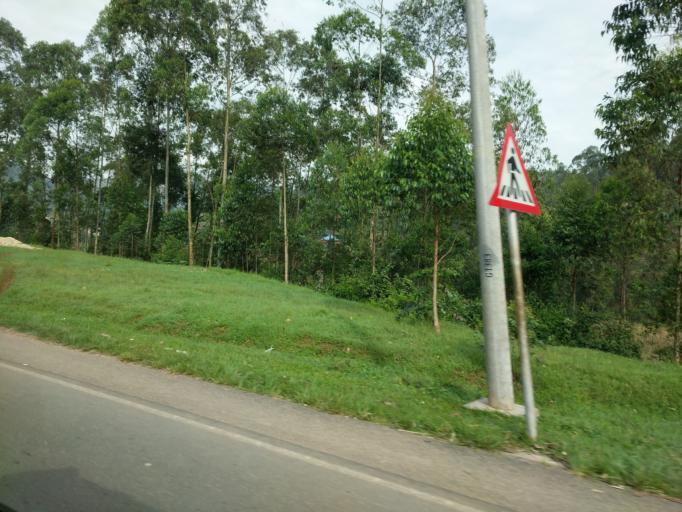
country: RW
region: Northern Province
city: Musanze
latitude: -1.6481
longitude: 29.8017
